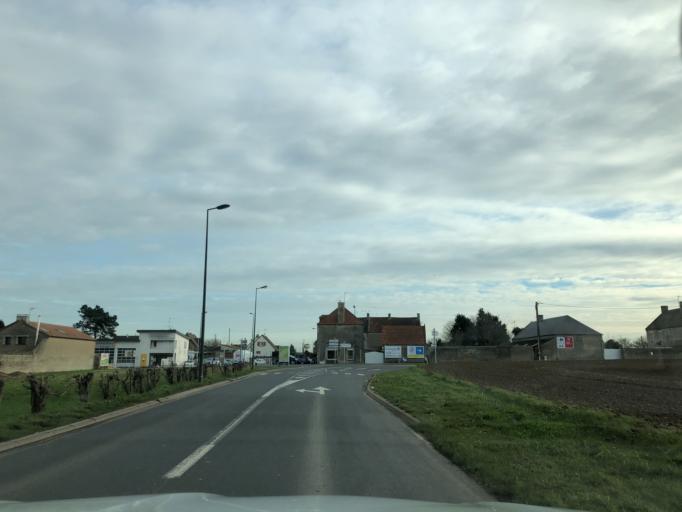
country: FR
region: Lower Normandy
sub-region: Departement du Calvados
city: Hermanville-sur-Mer
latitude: 49.2811
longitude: -0.3188
